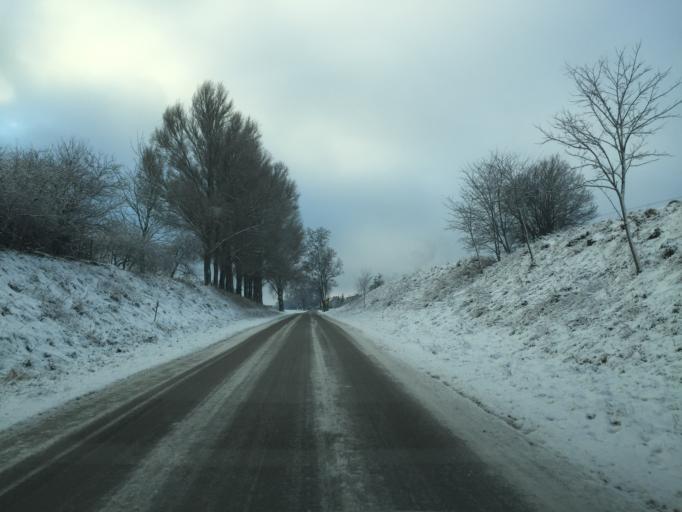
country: PL
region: Kujawsko-Pomorskie
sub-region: Powiat brodnicki
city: Bartniczka
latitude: 53.2546
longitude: 19.6319
